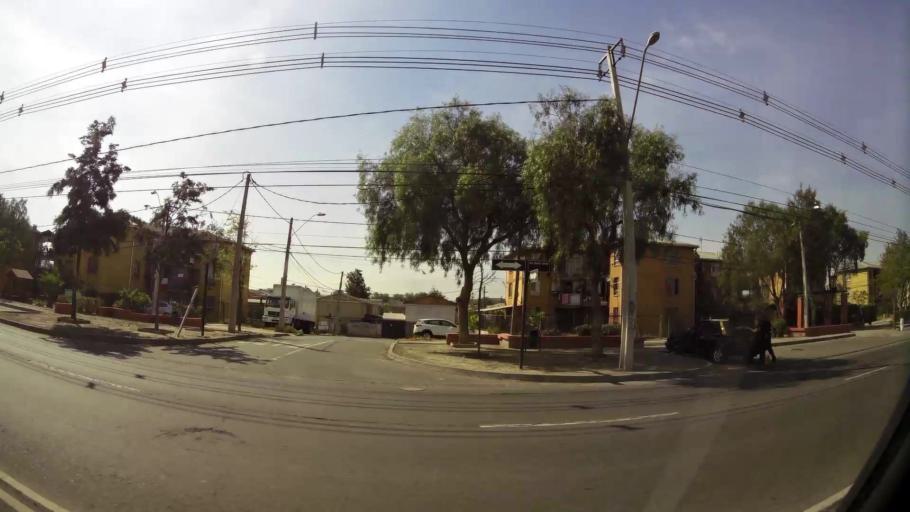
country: CL
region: Santiago Metropolitan
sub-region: Provincia de Santiago
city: Lo Prado
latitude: -33.4402
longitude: -70.7731
